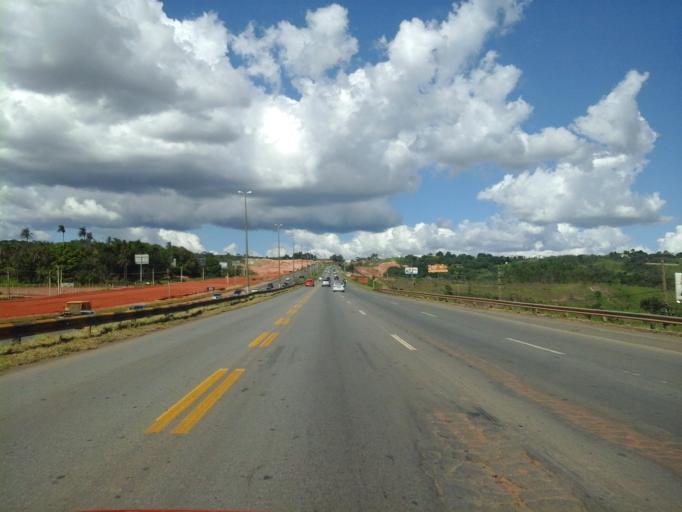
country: BR
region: Federal District
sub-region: Brasilia
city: Brasilia
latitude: -15.7063
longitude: -47.8910
